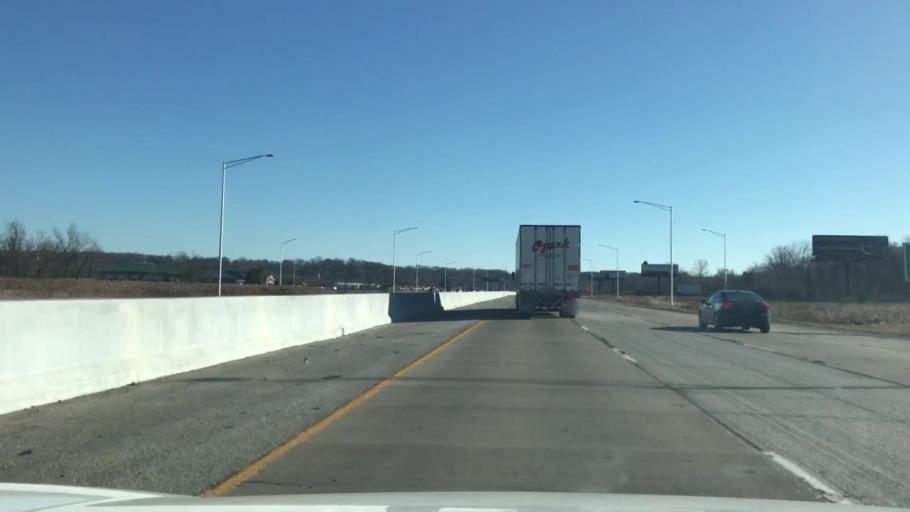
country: US
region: Illinois
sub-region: Saint Clair County
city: Alorton
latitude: 38.5817
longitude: -90.1071
